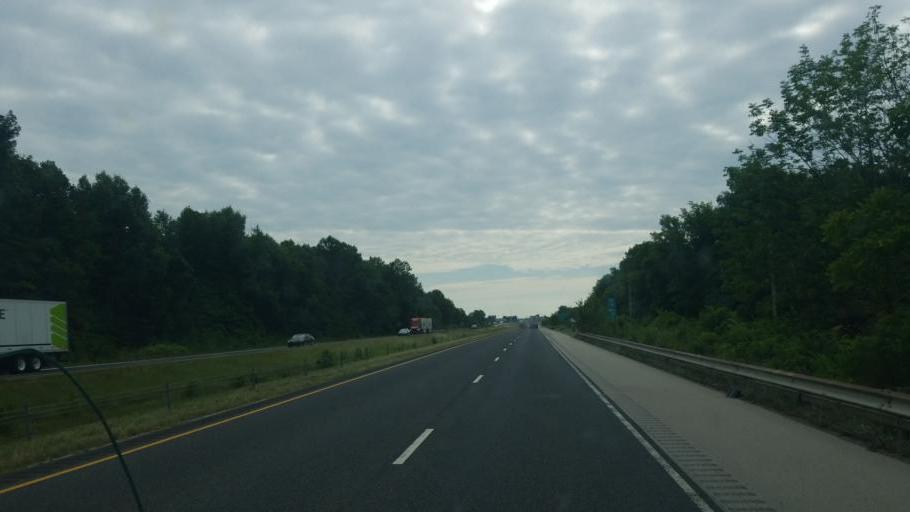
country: US
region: Indiana
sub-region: Vigo County
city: Terre Haute
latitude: 39.4306
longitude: -87.3560
